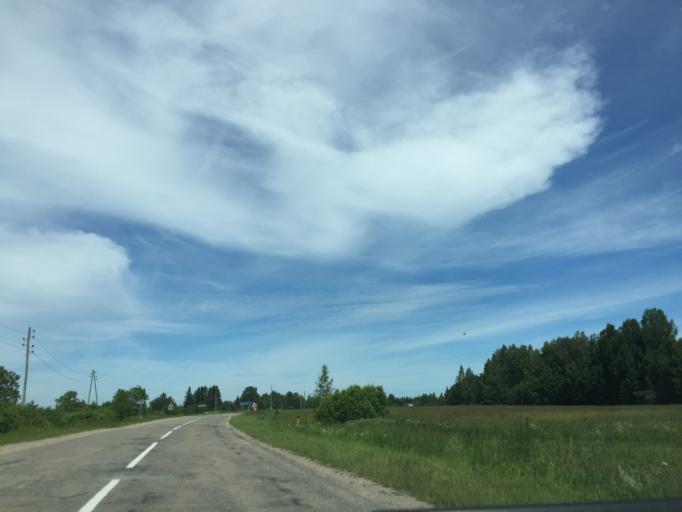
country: LV
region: Dundaga
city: Dundaga
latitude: 57.5210
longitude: 22.3343
